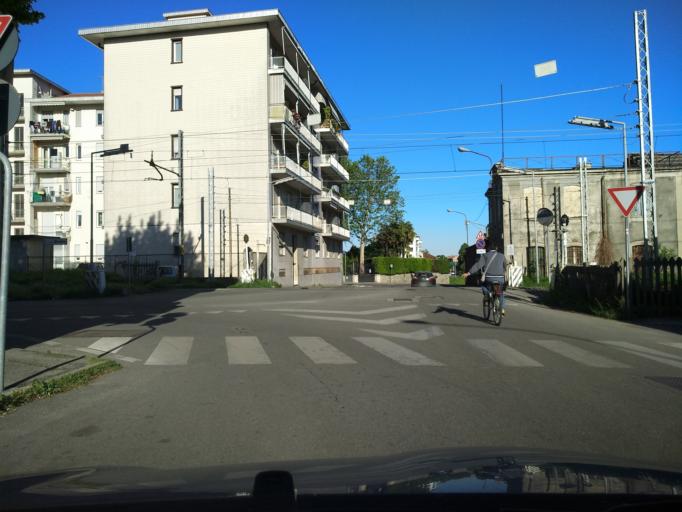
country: IT
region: Piedmont
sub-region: Provincia di Torino
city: Pinerolo
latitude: 44.8839
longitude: 7.3386
